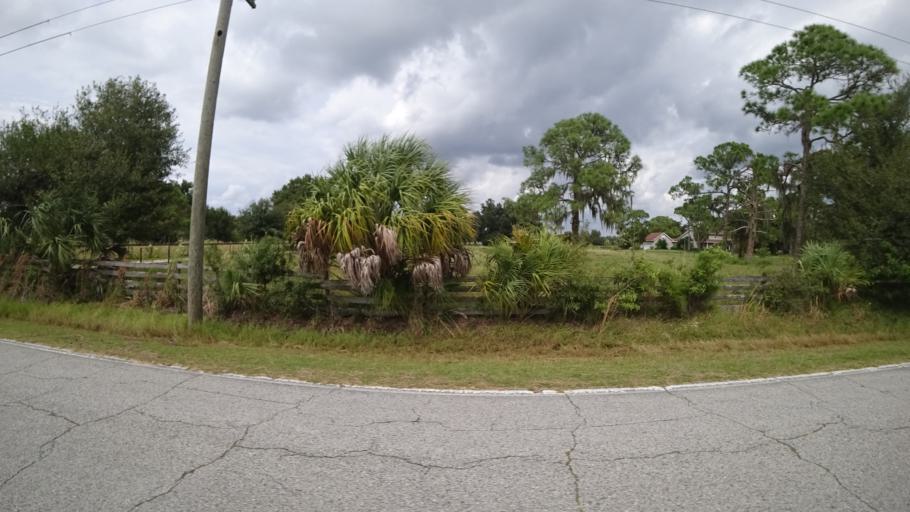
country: US
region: Florida
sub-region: Manatee County
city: Ellenton
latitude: 27.4878
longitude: -82.3850
